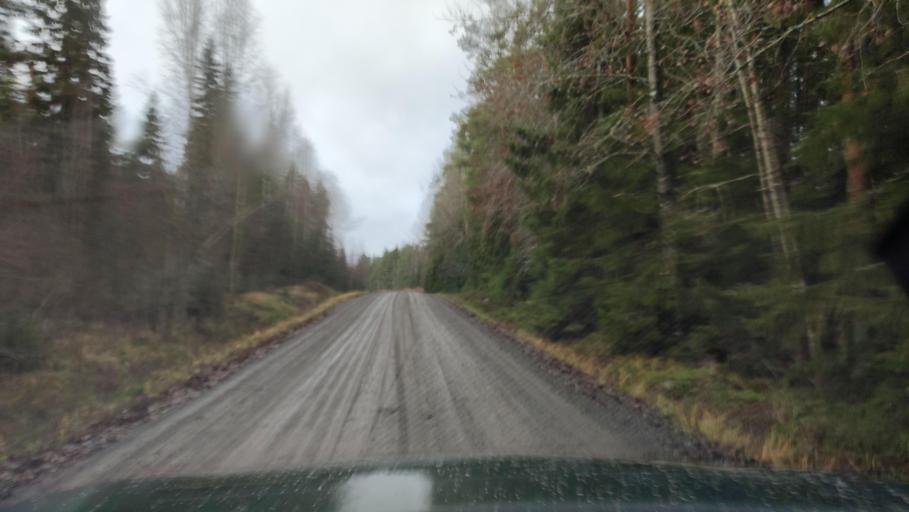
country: FI
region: Ostrobothnia
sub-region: Sydosterbotten
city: Naerpes
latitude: 62.4561
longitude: 21.5127
